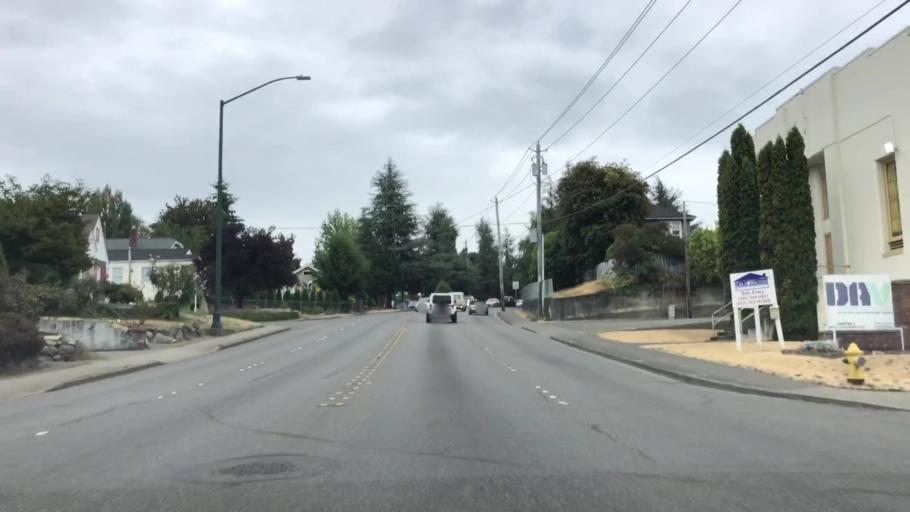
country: US
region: Washington
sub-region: Kitsap County
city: Bremerton
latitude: 47.5655
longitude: -122.6500
